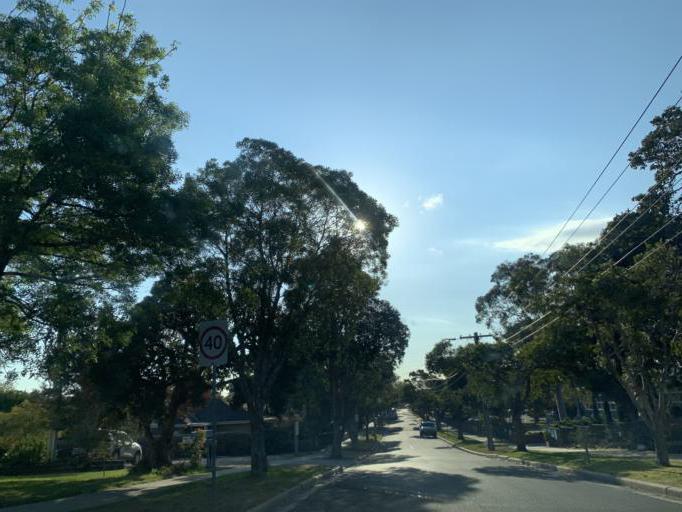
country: AU
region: Victoria
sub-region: Kingston
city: Mordialloc
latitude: -37.9873
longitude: 145.0887
